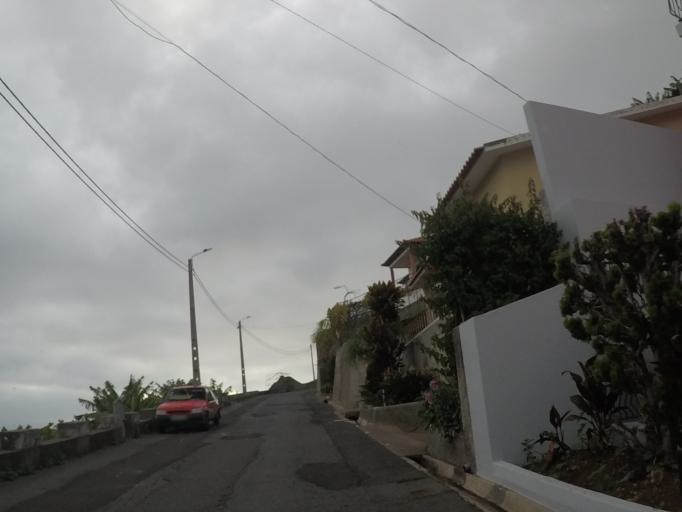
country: PT
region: Madeira
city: Camara de Lobos
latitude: 32.6519
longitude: -16.9724
